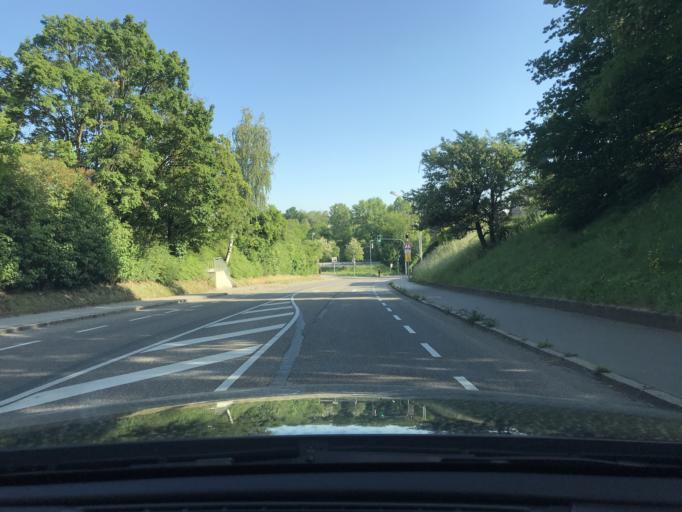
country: DE
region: Baden-Wuerttemberg
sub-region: Regierungsbezirk Stuttgart
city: Waiblingen
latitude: 48.8548
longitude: 9.3266
